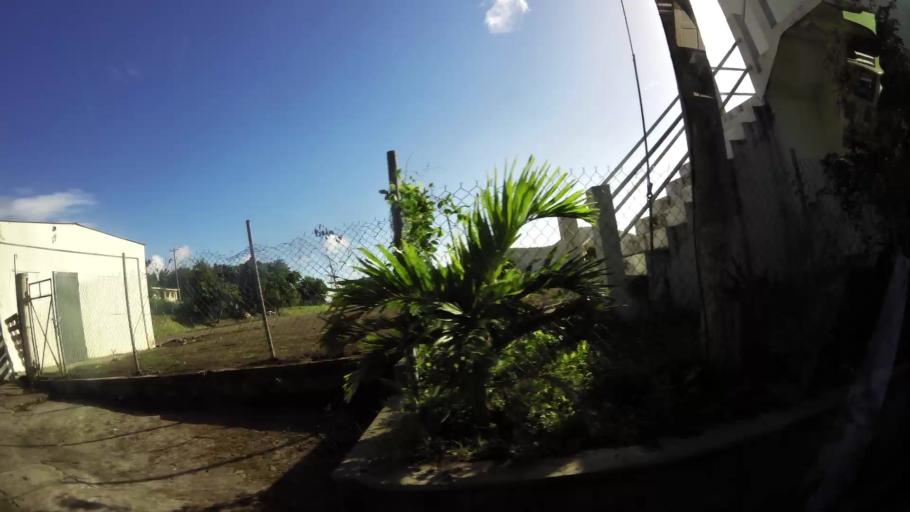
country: MS
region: Saint Peter
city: Saint Peters
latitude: 16.7483
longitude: -62.2224
